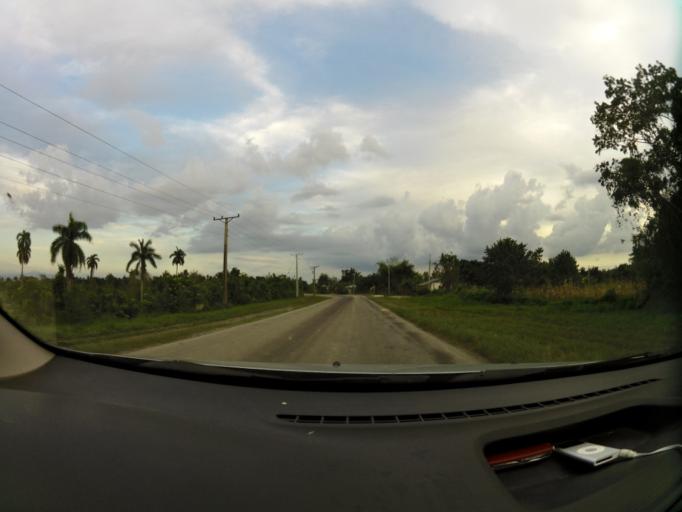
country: CU
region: Santiago de Cuba
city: Palma Soriano
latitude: 20.2304
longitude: -76.0801
